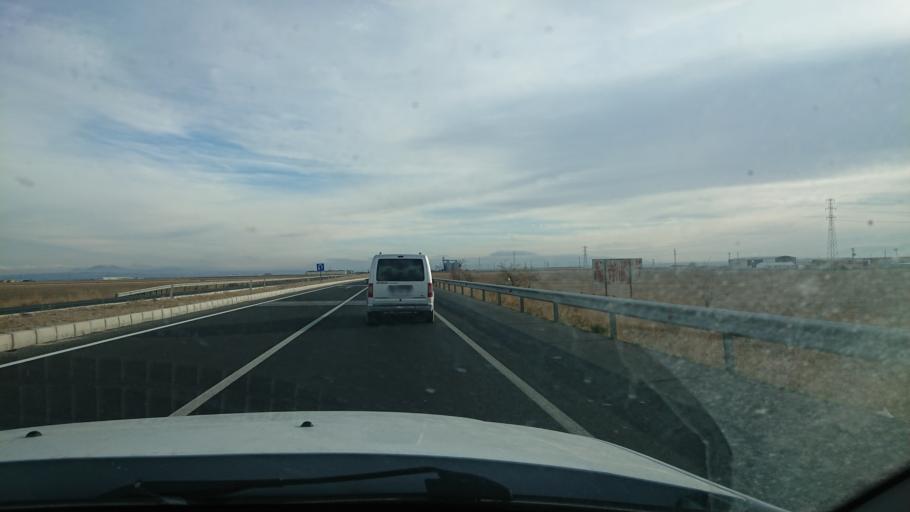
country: TR
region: Aksaray
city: Yesilova
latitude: 38.3033
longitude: 33.8066
